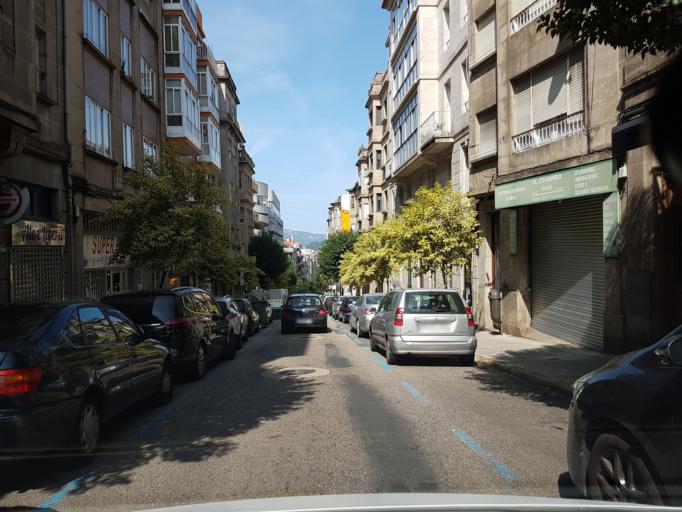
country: ES
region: Galicia
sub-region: Provincia de Pontevedra
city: Vigo
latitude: 42.2307
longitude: -8.7168
